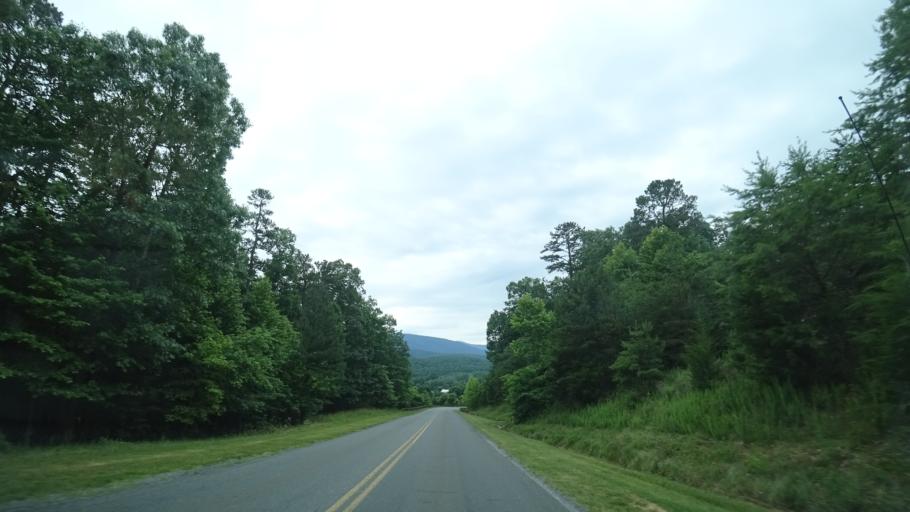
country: US
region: Virginia
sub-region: Warren County
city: Front Royal
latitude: 38.8428
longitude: -78.3010
